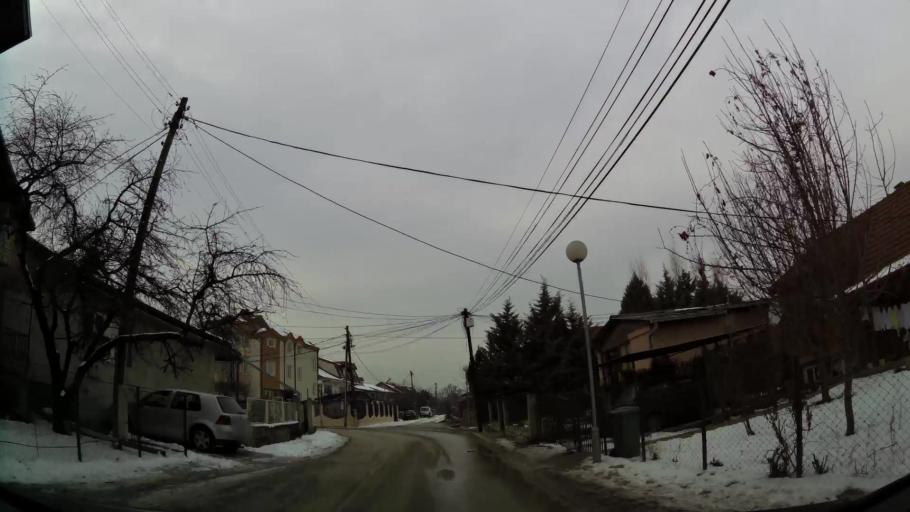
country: MK
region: Butel
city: Butel
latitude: 42.0388
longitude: 21.4533
